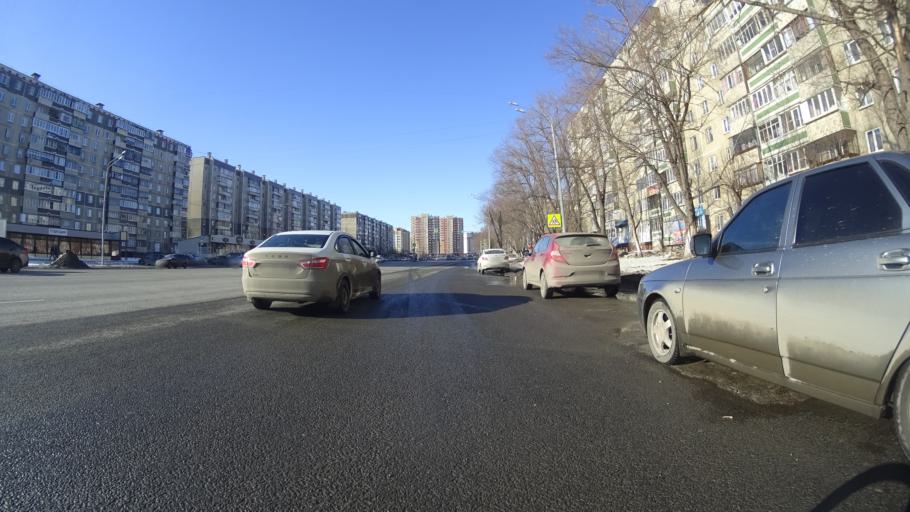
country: RU
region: Chelyabinsk
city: Roshchino
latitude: 55.1884
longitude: 61.2848
